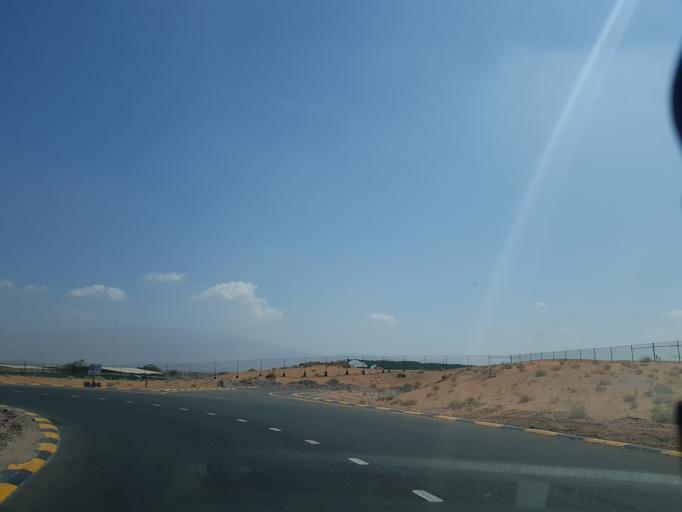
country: AE
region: Ra's al Khaymah
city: Ras al-Khaimah
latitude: 25.6922
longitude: 55.9279
